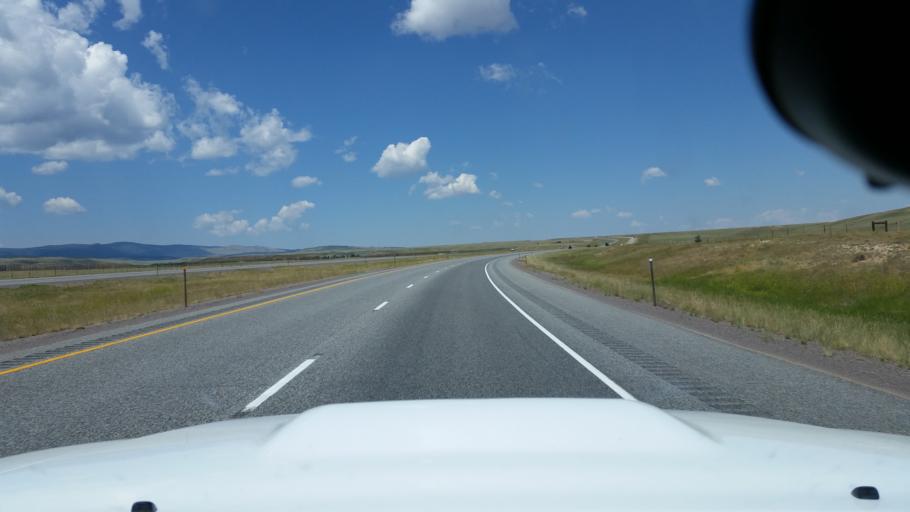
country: US
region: Wyoming
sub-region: Albany County
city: Laramie
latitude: 41.4457
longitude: -105.9655
